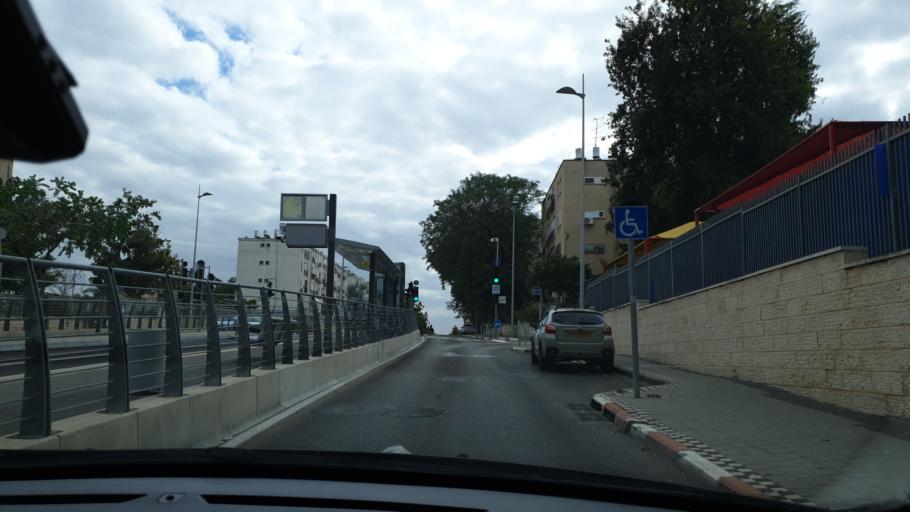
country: IL
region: Haifa
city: Qiryat Ata
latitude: 32.8105
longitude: 35.1150
